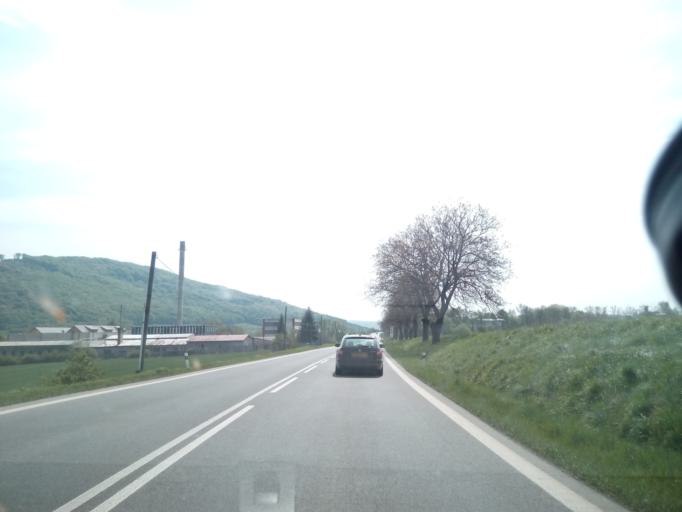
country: SK
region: Presovsky
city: Giraltovce
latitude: 49.0314
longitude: 21.5197
